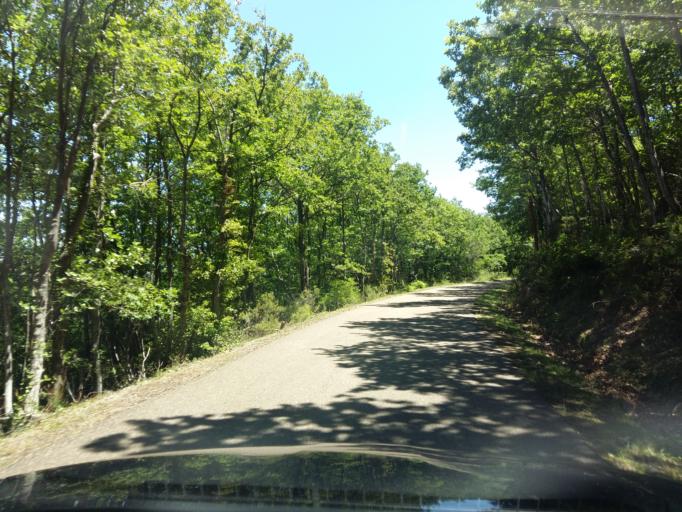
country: ES
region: Aragon
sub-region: Provincia de Zaragoza
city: Litago
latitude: 41.7962
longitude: -1.7839
